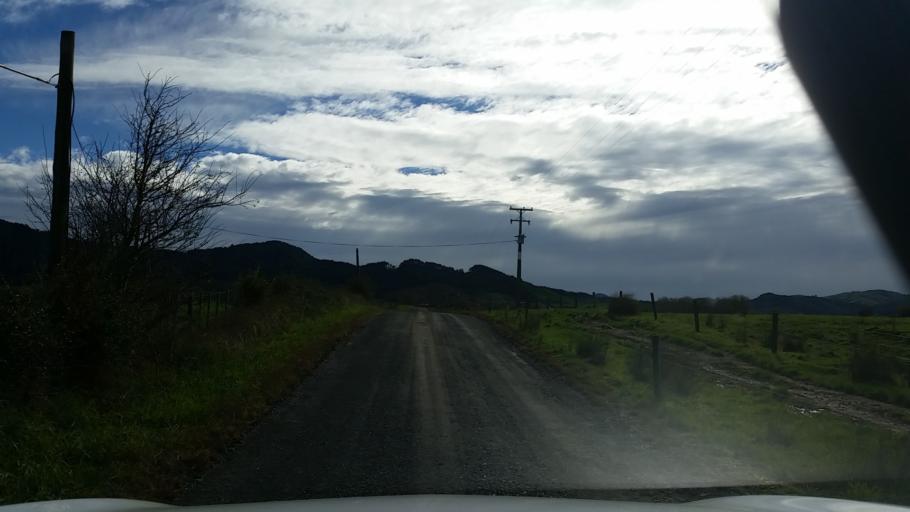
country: NZ
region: Waikato
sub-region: Hauraki District
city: Ngatea
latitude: -37.5116
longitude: 175.4088
